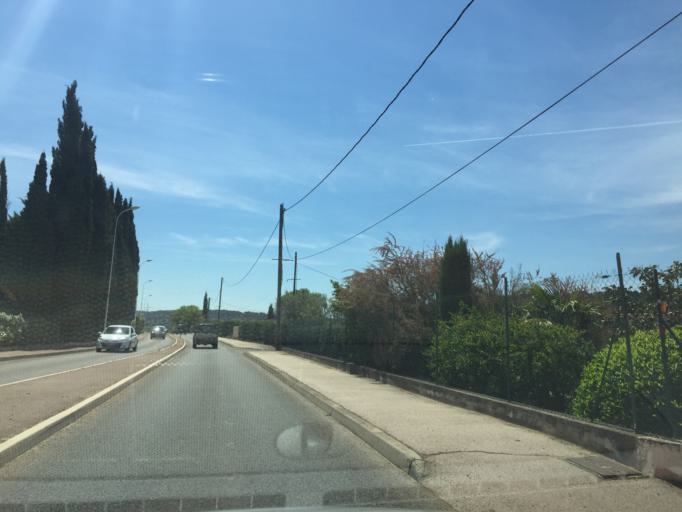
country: FR
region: Provence-Alpes-Cote d'Azur
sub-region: Departement du Var
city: Lorgues
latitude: 43.4880
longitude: 6.3652
